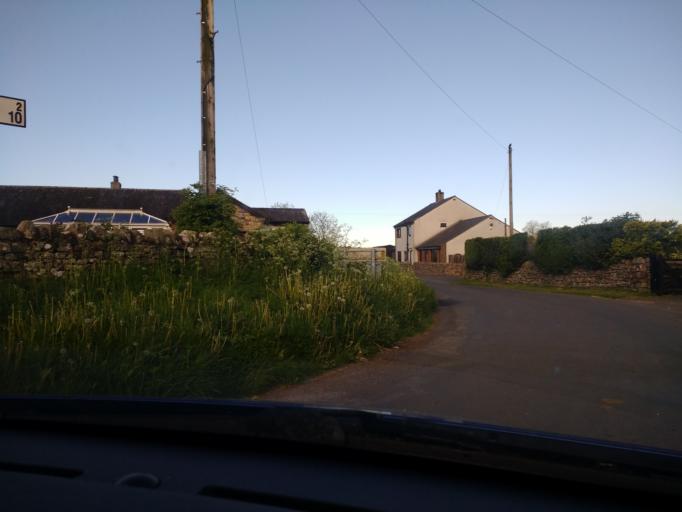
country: GB
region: England
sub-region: Cumbria
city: Appleby-in-Westmorland
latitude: 54.6750
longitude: -2.5657
